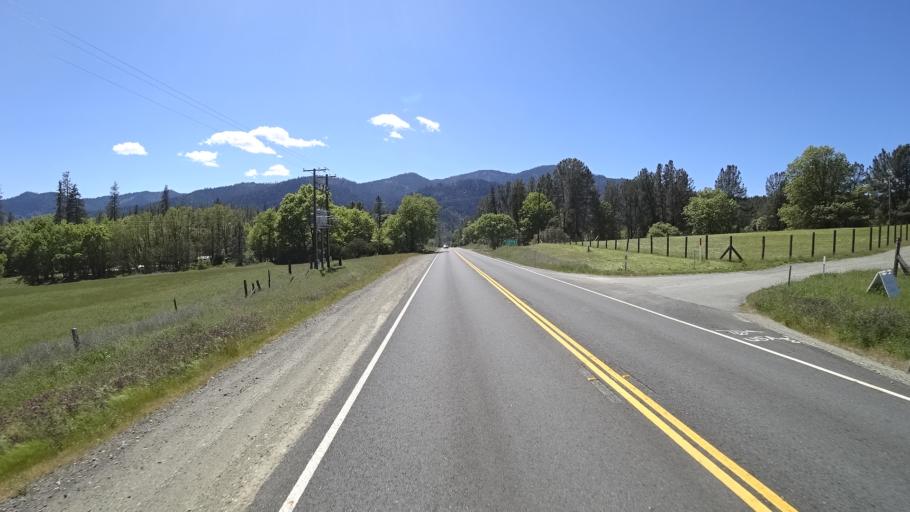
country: US
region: California
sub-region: Trinity County
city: Weaverville
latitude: 40.7282
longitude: -123.0400
